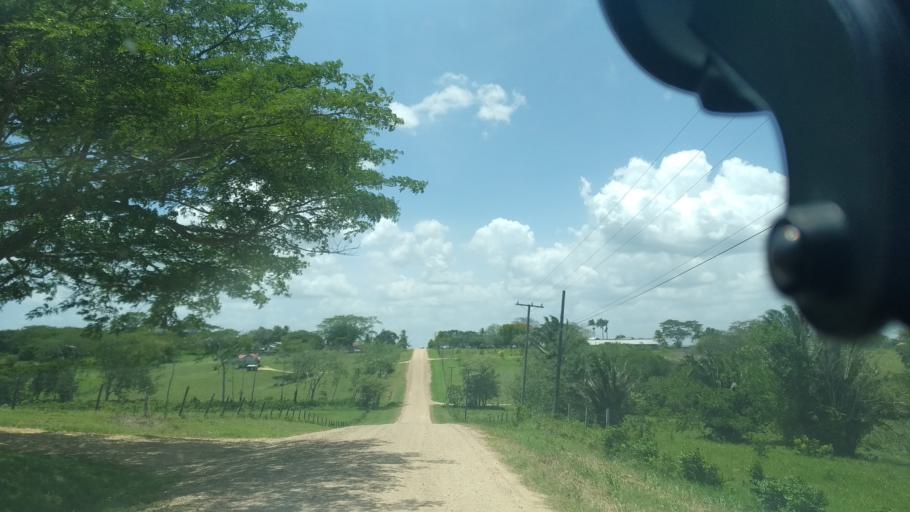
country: BZ
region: Cayo
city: San Ignacio
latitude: 17.2391
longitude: -88.9875
